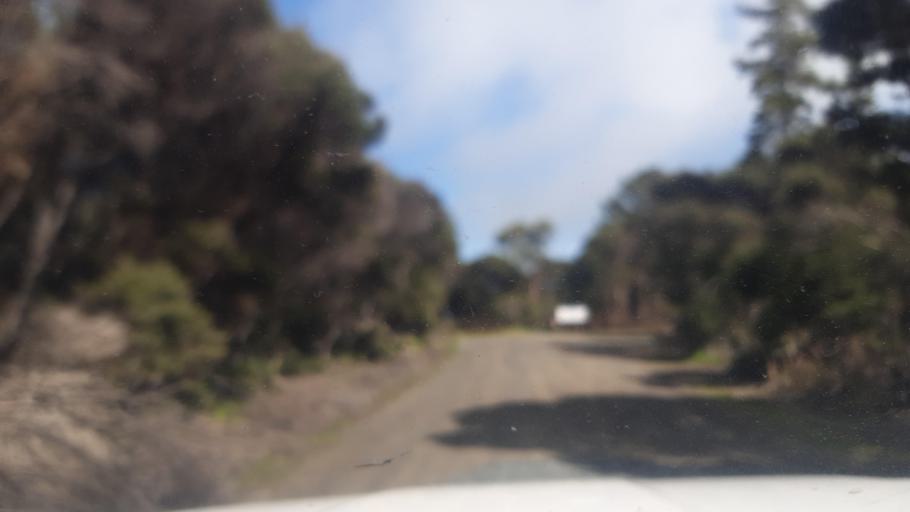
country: NZ
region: Northland
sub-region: Far North District
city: Kaitaia
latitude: -34.7371
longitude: 173.1056
